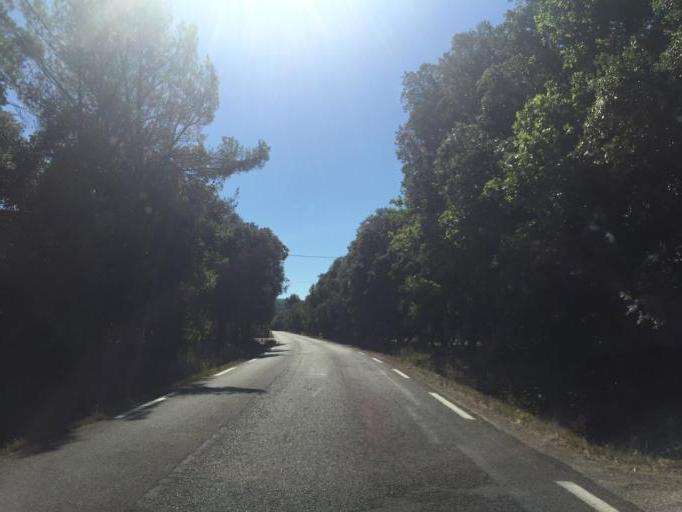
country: FR
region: Provence-Alpes-Cote d'Azur
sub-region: Departement du Vaucluse
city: Saint-Didier
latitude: 44.0164
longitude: 5.1293
